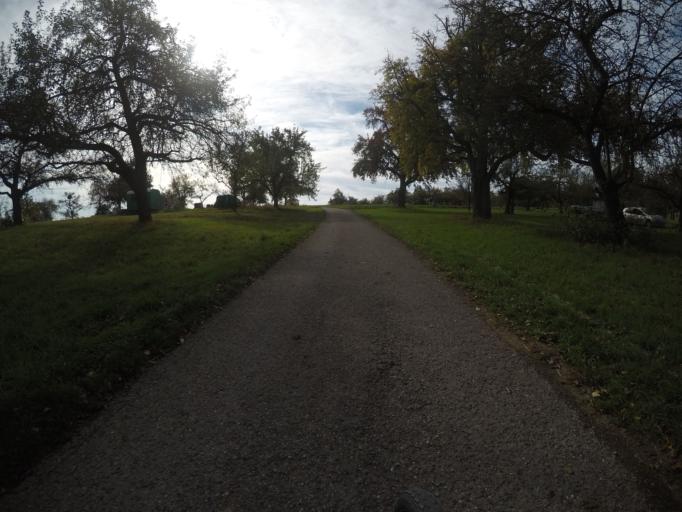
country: DE
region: Baden-Wuerttemberg
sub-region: Regierungsbezirk Stuttgart
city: Gartringen
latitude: 48.6559
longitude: 8.9057
